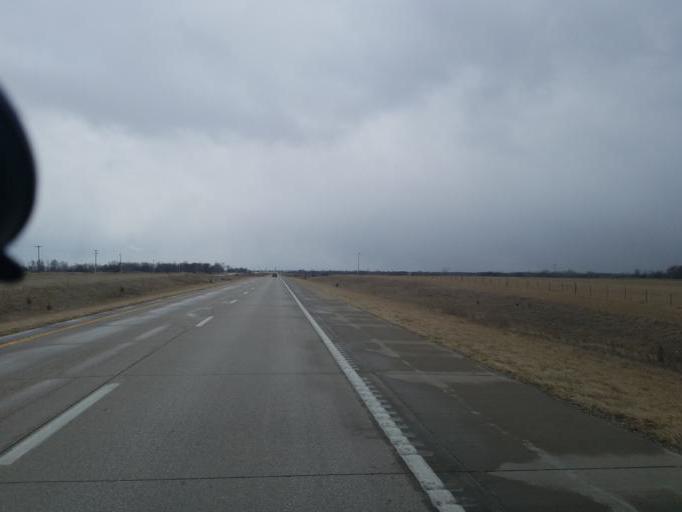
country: US
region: Missouri
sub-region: Randolph County
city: Moberly
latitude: 39.4855
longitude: -92.4345
